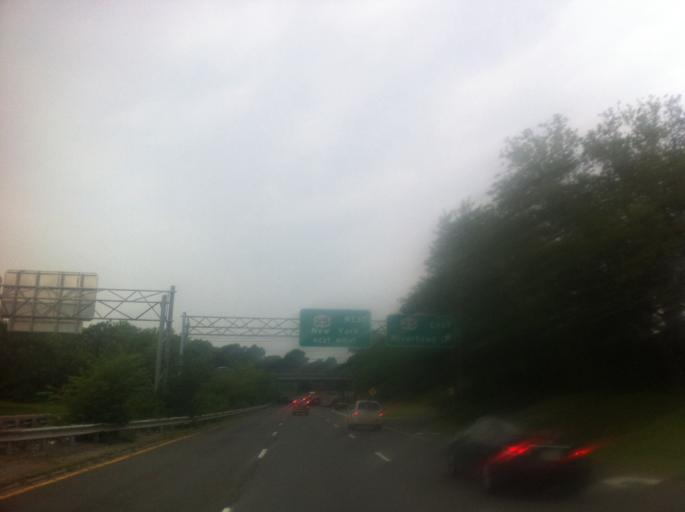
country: US
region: New York
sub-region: Nassau County
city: Jericho
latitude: 40.7879
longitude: -73.5353
